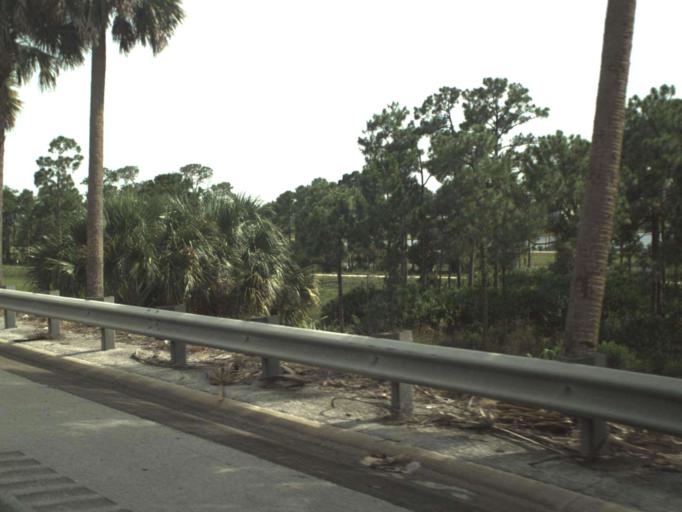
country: US
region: Florida
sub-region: Saint Lucie County
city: Port Saint Lucie
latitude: 27.2628
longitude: -80.4218
